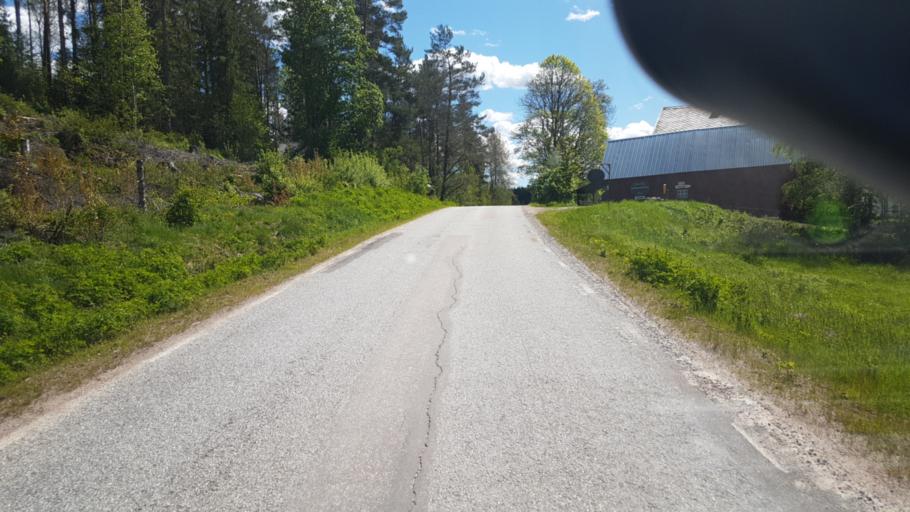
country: SE
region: Vaermland
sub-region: Sunne Kommun
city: Sunne
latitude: 59.6720
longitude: 12.9046
